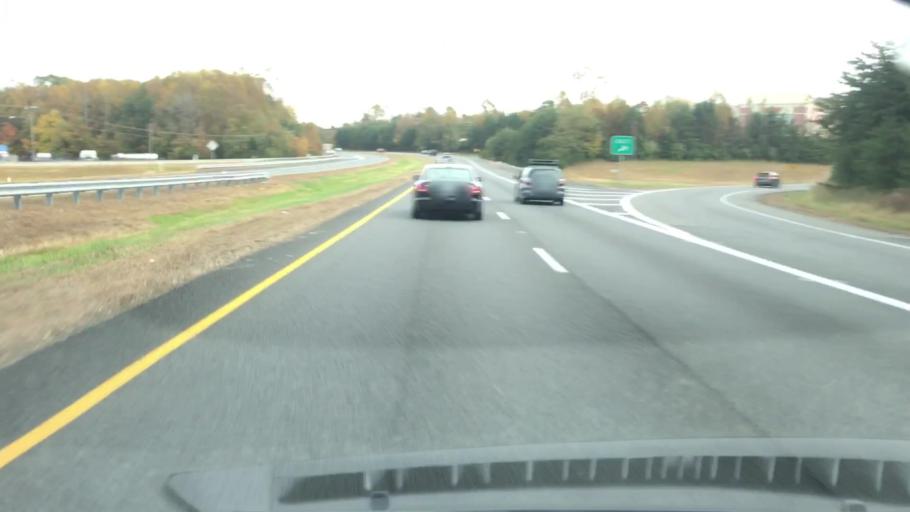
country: US
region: Virginia
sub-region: Fairfax County
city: Fairfax Station
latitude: 38.7882
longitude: -77.3264
